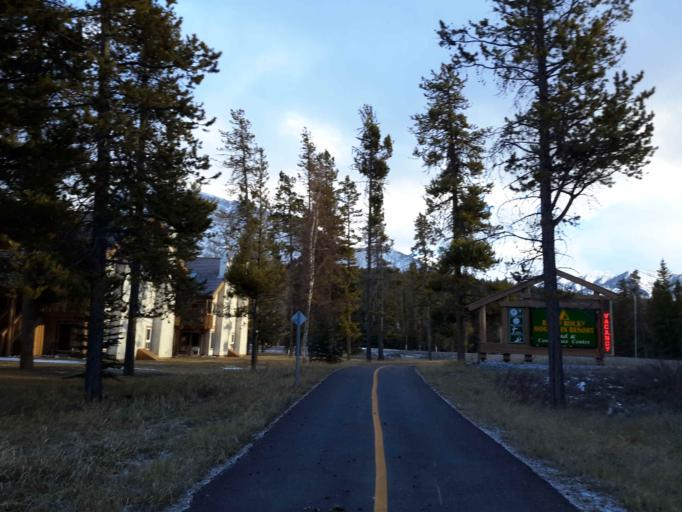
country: CA
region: Alberta
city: Banff
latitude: 51.2012
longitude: -115.5370
